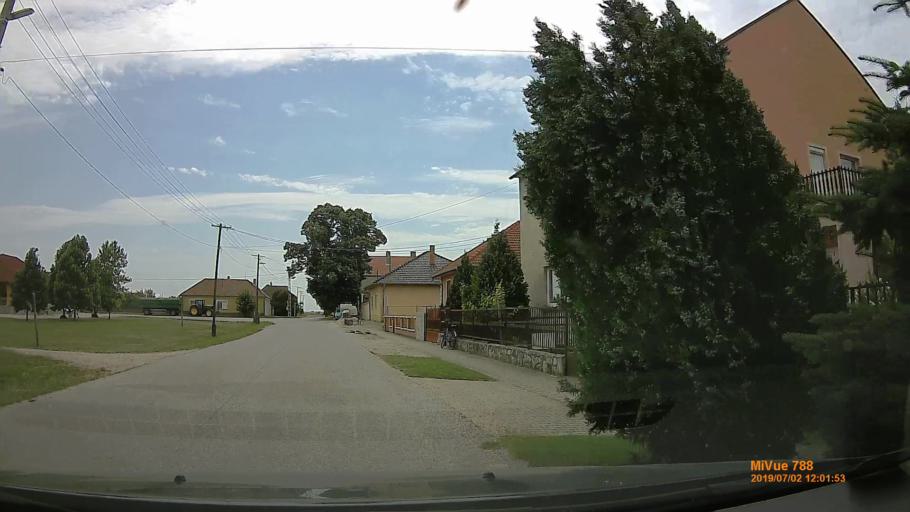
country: HU
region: Gyor-Moson-Sopron
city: Janossomorja
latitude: 47.8478
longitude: 17.1728
